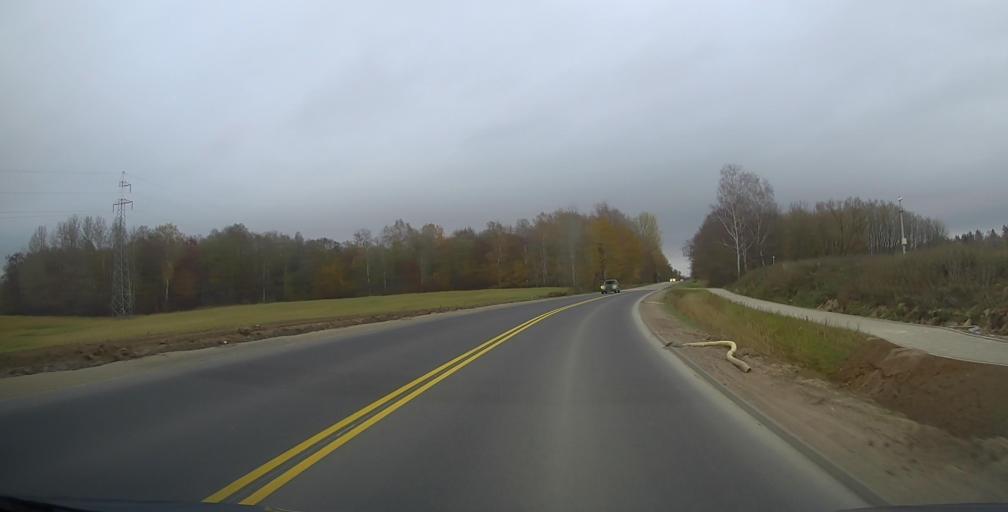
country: PL
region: Warmian-Masurian Voivodeship
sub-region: Powiat elcki
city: Elk
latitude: 53.8572
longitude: 22.5001
